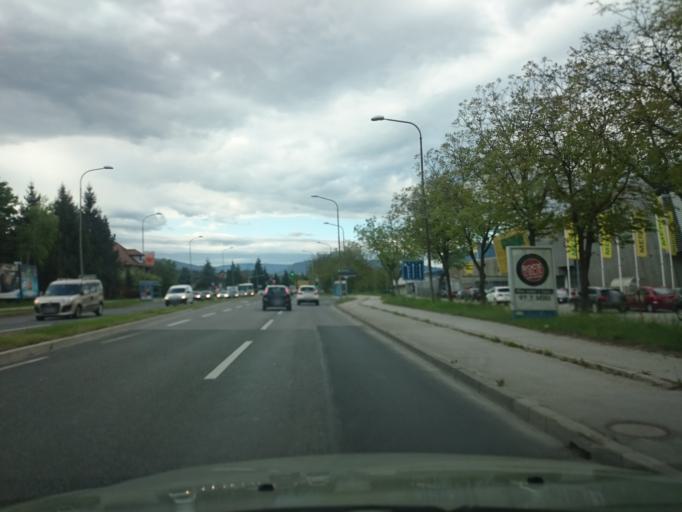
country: SI
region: Celje
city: Trnovlje pri Celju
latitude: 46.2492
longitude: 15.2801
